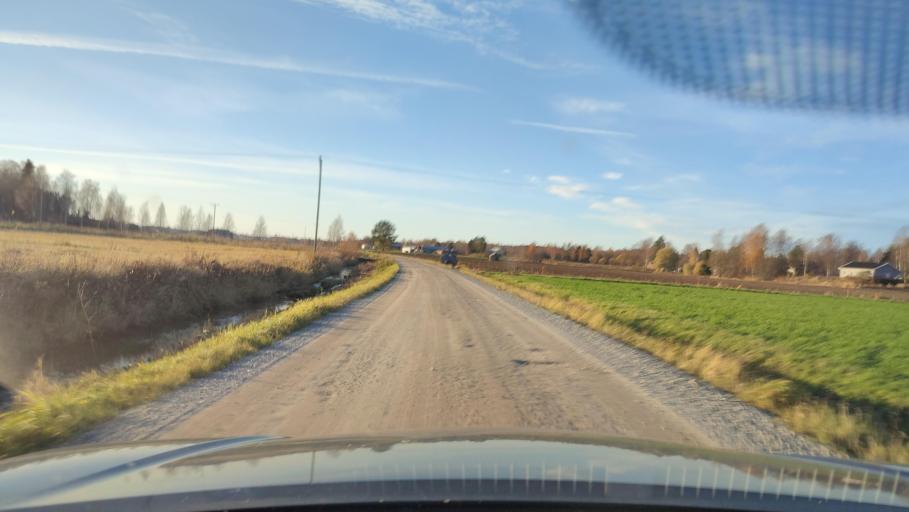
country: FI
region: Ostrobothnia
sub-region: Vaasa
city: Ristinummi
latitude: 63.0095
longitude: 21.7113
